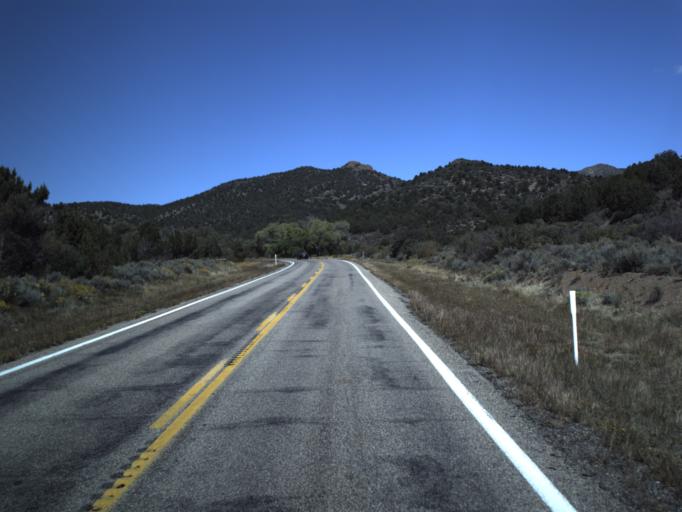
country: US
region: Utah
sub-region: Washington County
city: Enterprise
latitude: 37.4498
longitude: -113.6225
